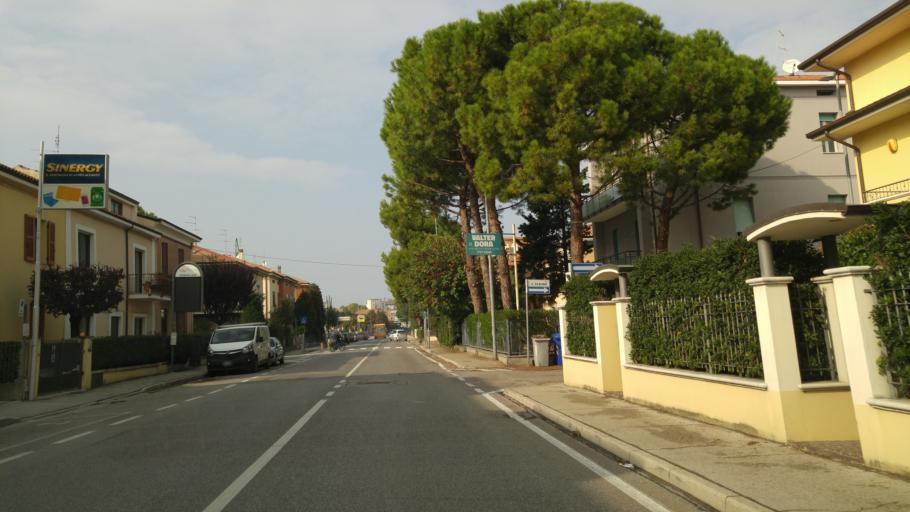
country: IT
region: The Marches
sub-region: Provincia di Pesaro e Urbino
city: Pesaro
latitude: 43.9017
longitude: 12.9188
